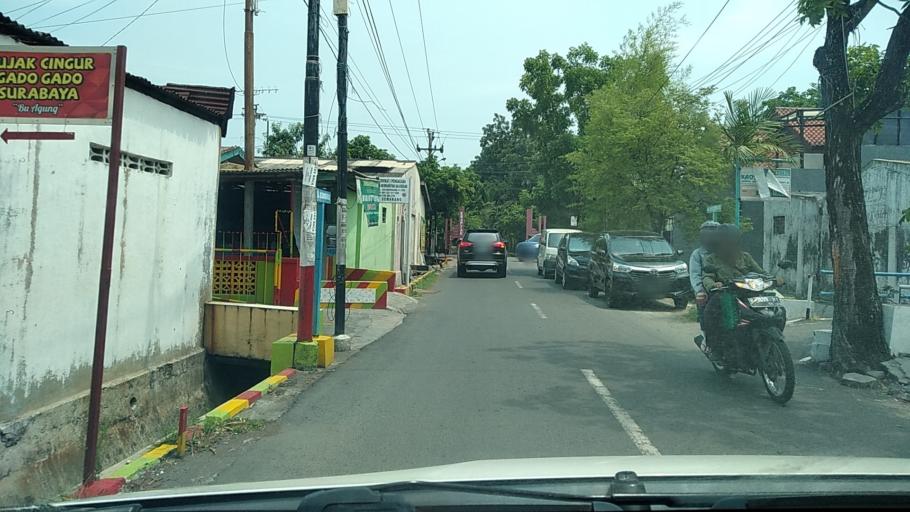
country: ID
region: Central Java
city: Semarang
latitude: -6.9838
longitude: 110.3688
